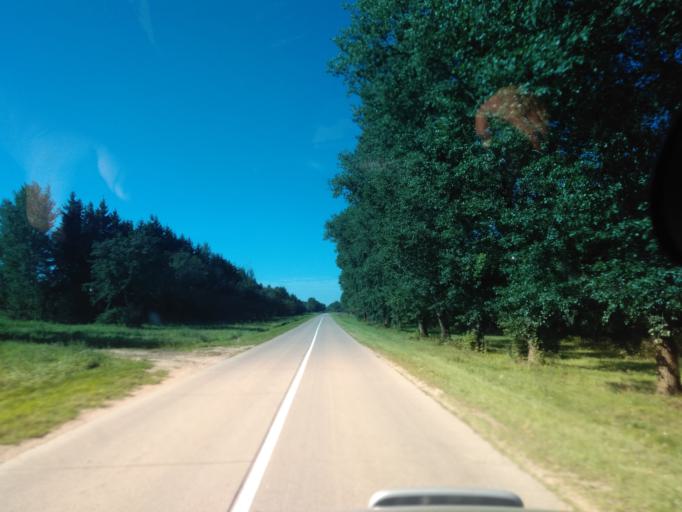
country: BY
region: Minsk
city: Stan'kava
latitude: 53.6524
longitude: 27.3105
